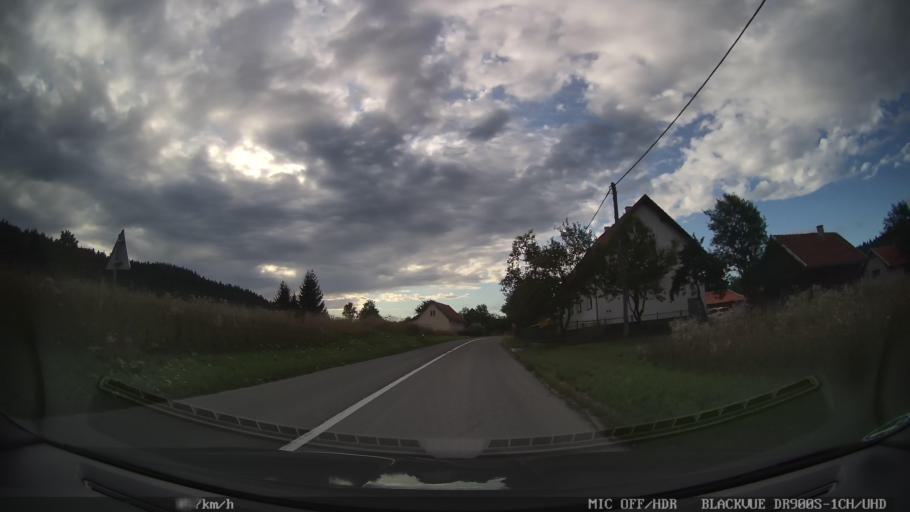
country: HR
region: Licko-Senjska
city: Jezerce
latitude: 44.9716
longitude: 15.5032
